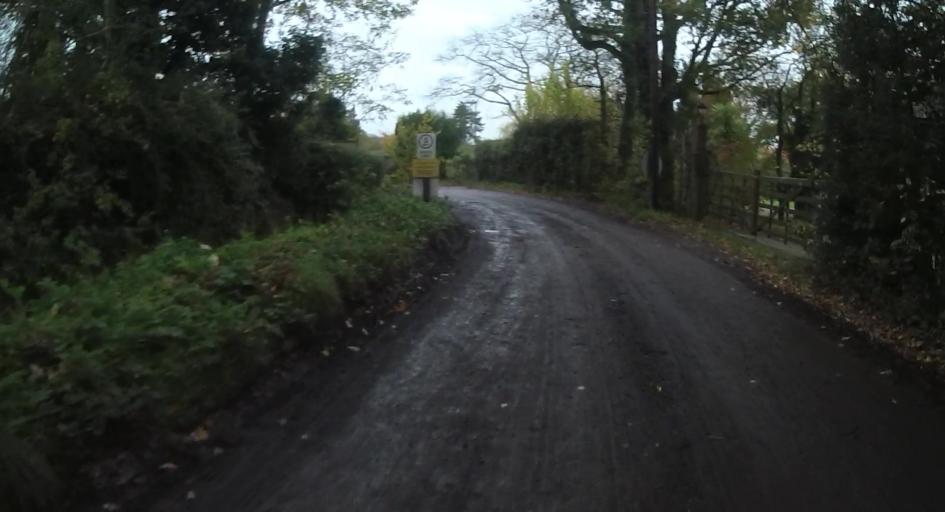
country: GB
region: England
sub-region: Surrey
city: Farnham
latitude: 51.2200
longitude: -0.8069
